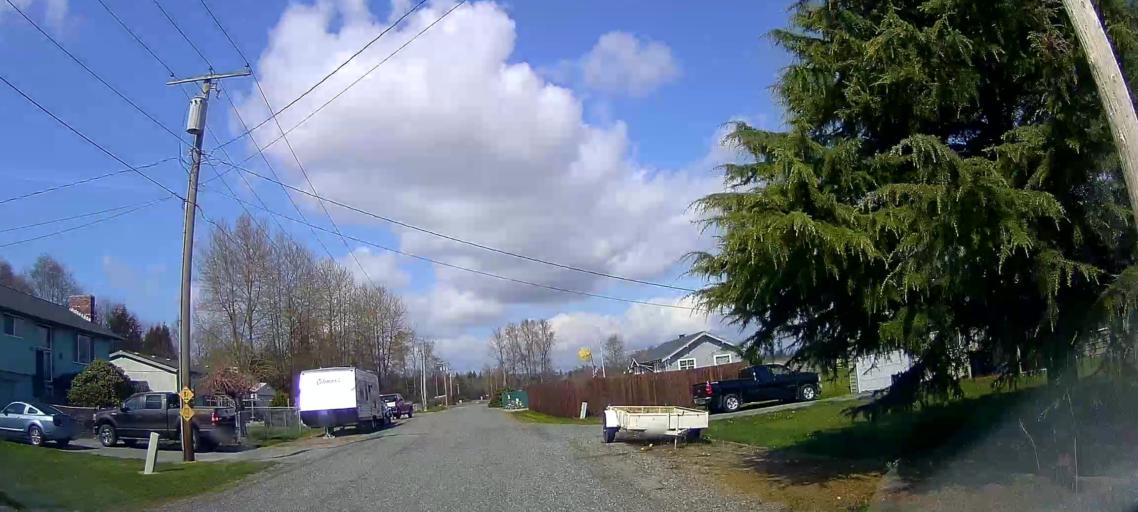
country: US
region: Washington
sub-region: Skagit County
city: Mount Vernon
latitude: 48.4463
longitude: -122.4220
